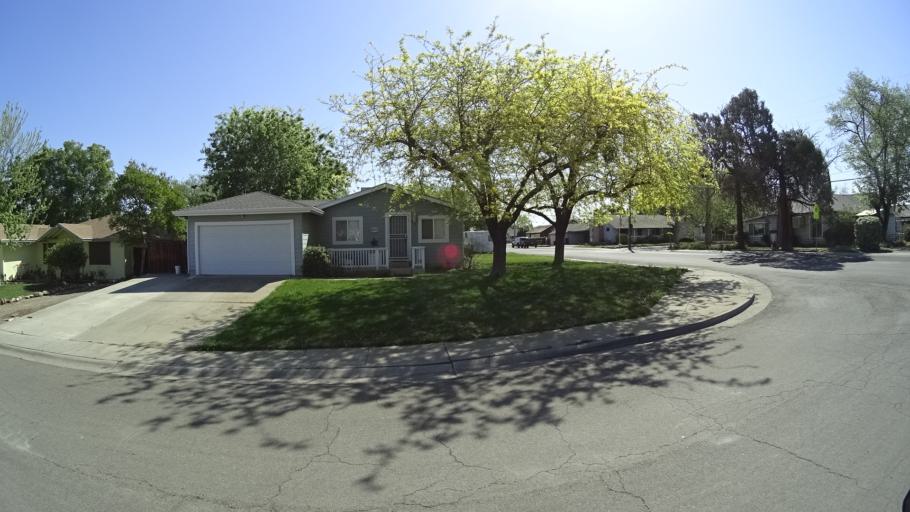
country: US
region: California
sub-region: Glenn County
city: Willows
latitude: 39.5292
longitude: -122.2027
